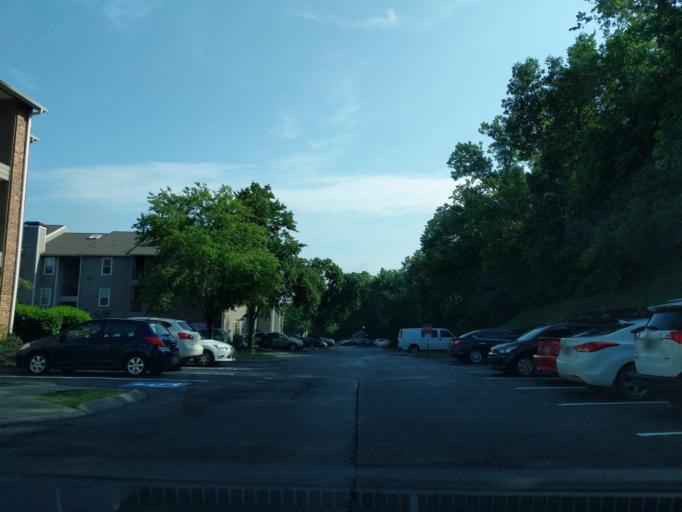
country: US
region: Tennessee
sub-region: Sumner County
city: Hendersonville
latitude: 36.3081
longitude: -86.6522
